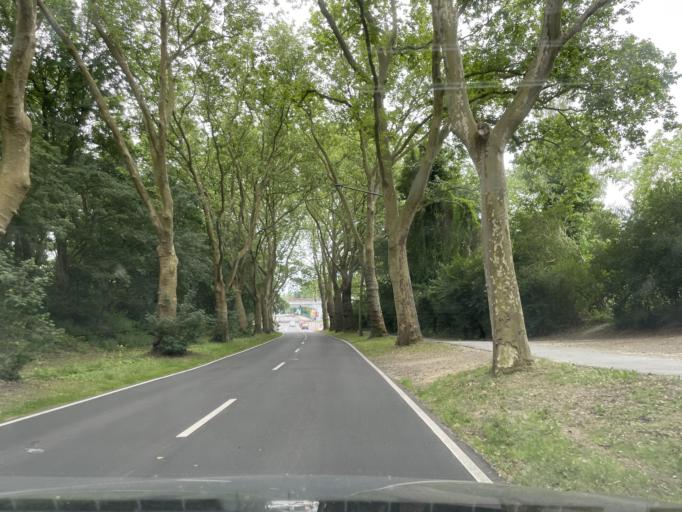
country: DE
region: North Rhine-Westphalia
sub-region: Regierungsbezirk Dusseldorf
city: Monchengladbach
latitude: 51.1520
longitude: 6.4275
